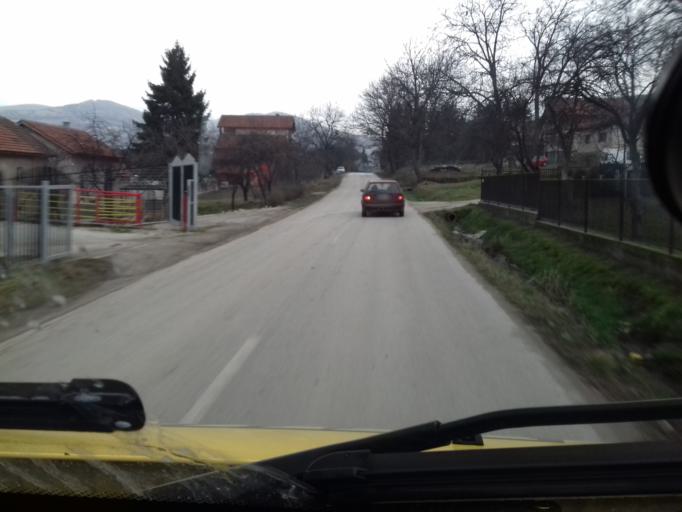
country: BA
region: Federation of Bosnia and Herzegovina
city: Zenica
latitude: 44.1816
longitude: 17.9601
